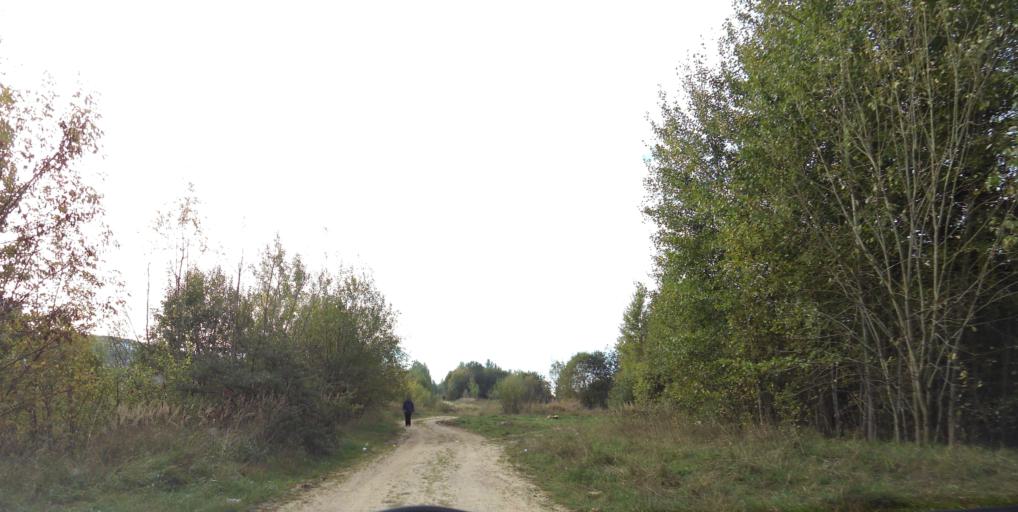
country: LT
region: Vilnius County
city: Justiniskes
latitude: 54.7187
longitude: 25.2103
